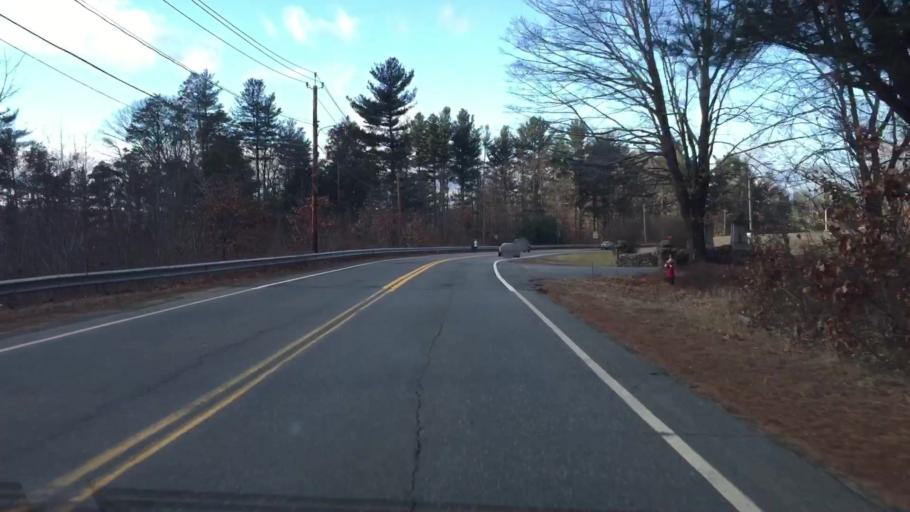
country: US
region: Massachusetts
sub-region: Worcester County
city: West Boylston
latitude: 42.3817
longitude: -71.7873
